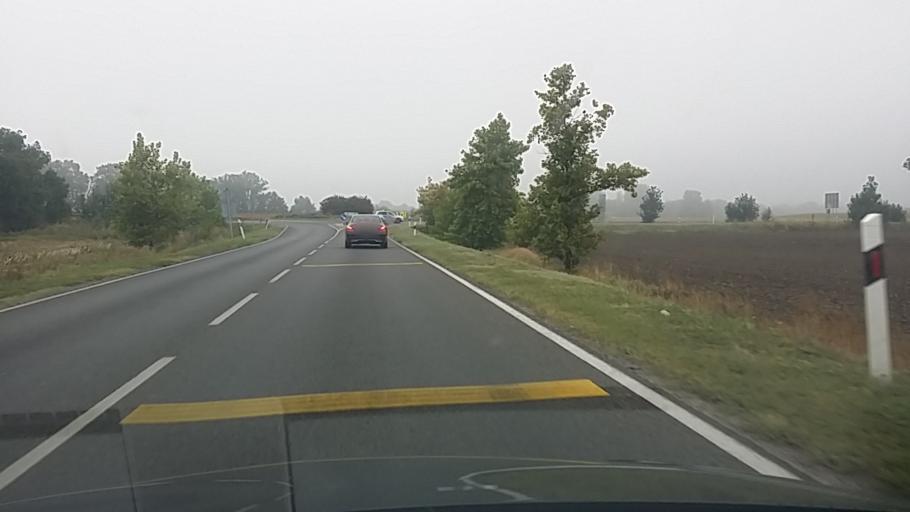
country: HU
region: Csongrad
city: Szeged
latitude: 46.2336
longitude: 20.0874
